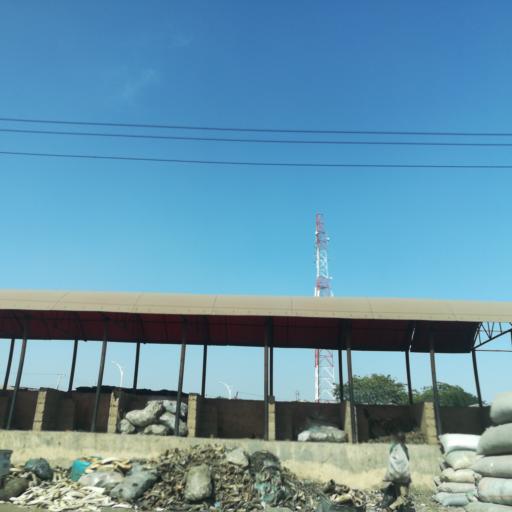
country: NG
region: Kano
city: Kano
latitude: 12.0116
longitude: 8.5216
